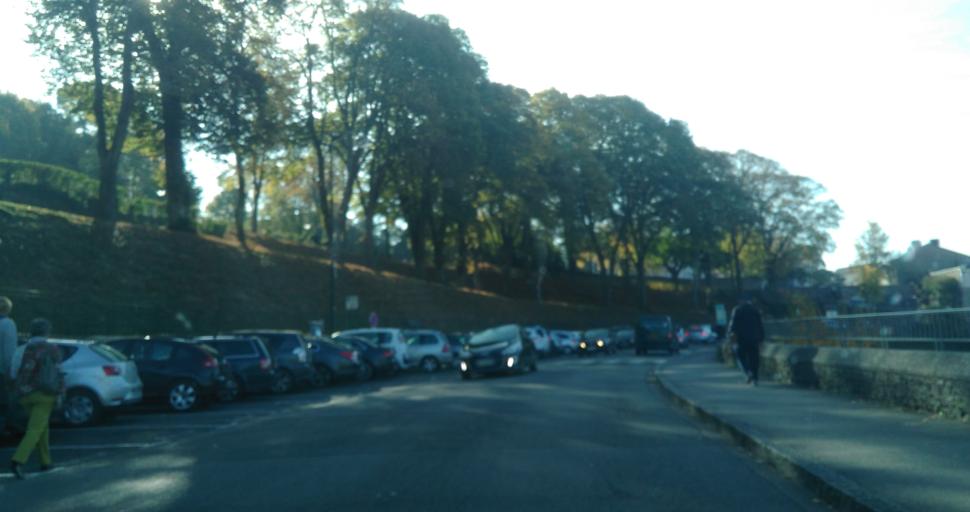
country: FR
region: Brittany
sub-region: Departement du Morbihan
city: Vannes
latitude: 47.6563
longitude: -2.7551
